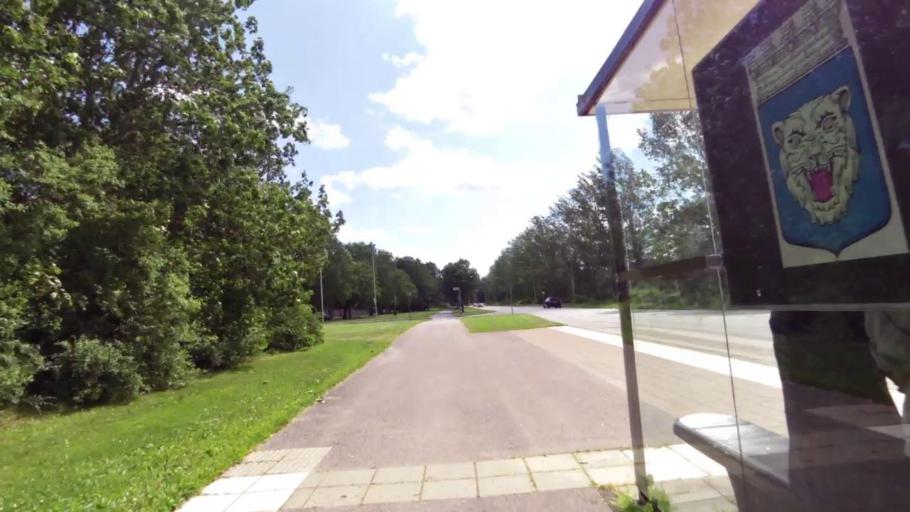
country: SE
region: OEstergoetland
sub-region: Linkopings Kommun
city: Malmslatt
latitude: 58.4297
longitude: 15.5678
